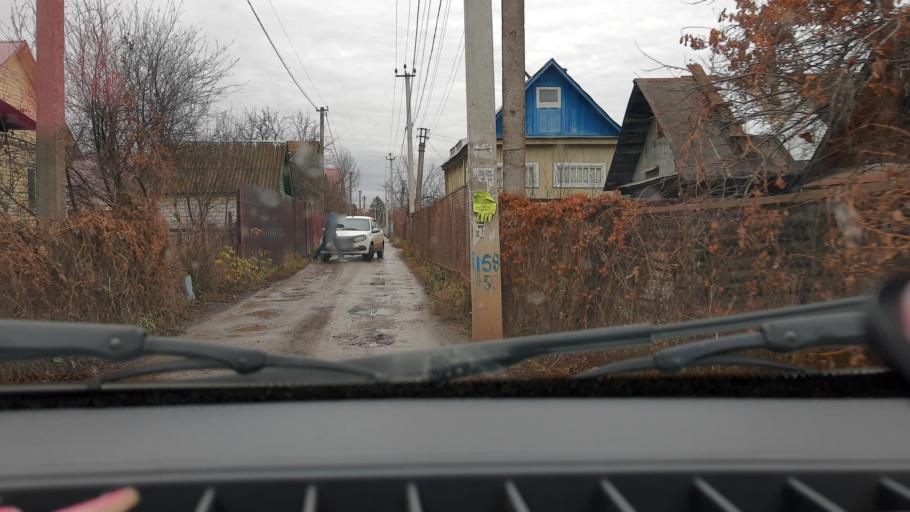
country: RU
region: Bashkortostan
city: Ufa
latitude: 54.6930
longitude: 55.8979
